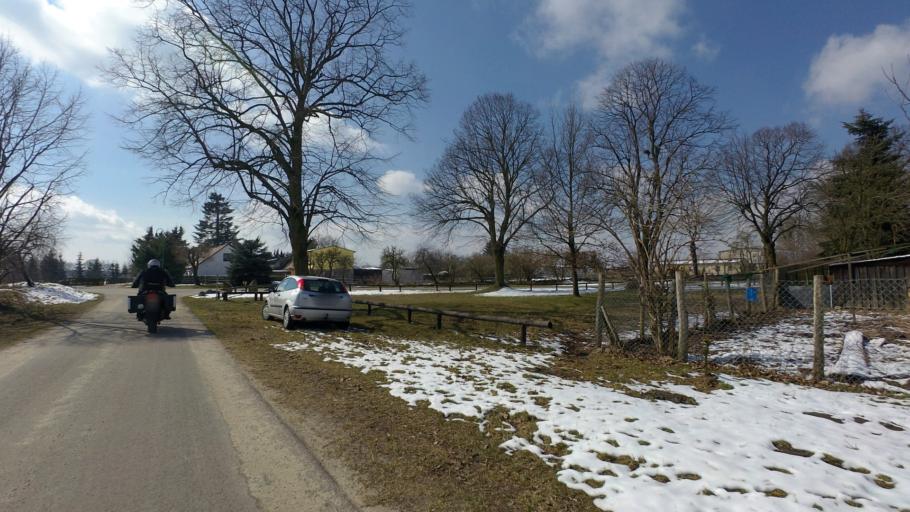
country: DE
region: Brandenburg
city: Werftpfuhl
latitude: 52.6967
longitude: 13.7788
